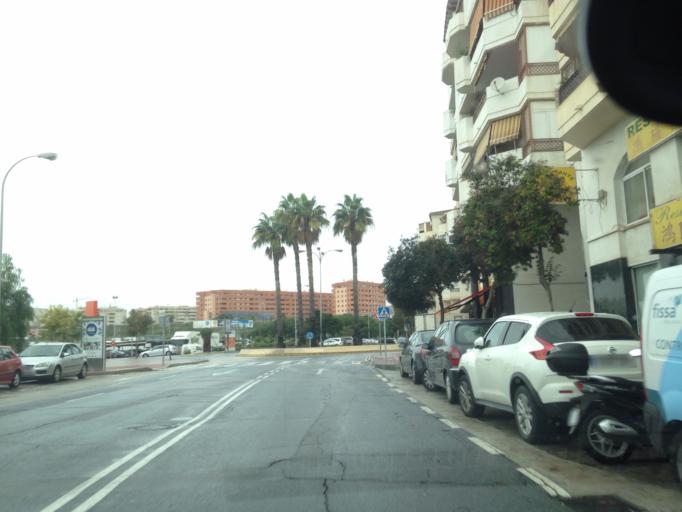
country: ES
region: Andalusia
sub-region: Provincia de Malaga
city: Malaga
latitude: 36.7164
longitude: -4.4558
